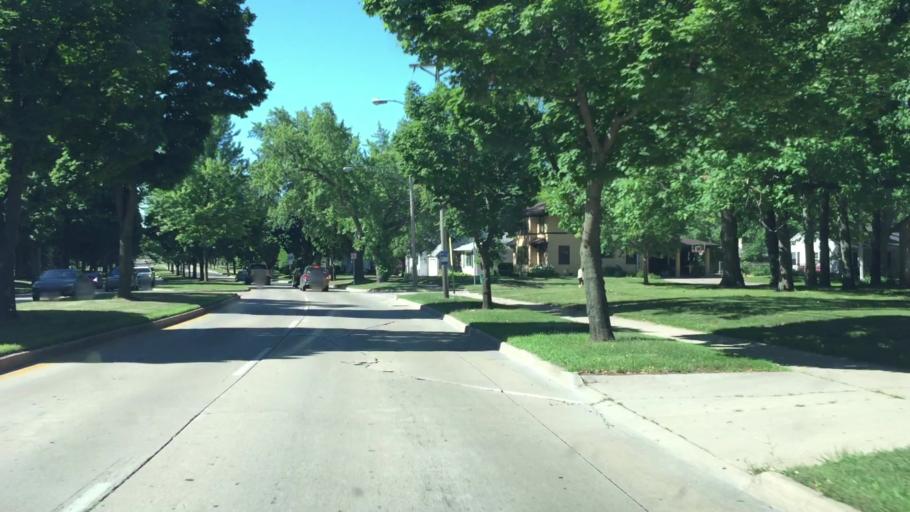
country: US
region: Wisconsin
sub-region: Outagamie County
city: Appleton
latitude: 44.2506
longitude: -88.4156
